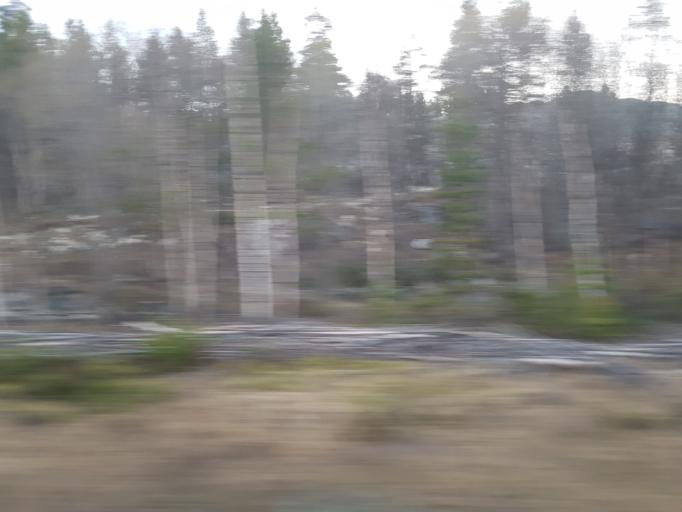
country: NO
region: Oppland
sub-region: Dovre
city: Dombas
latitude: 62.1106
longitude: 9.0975
